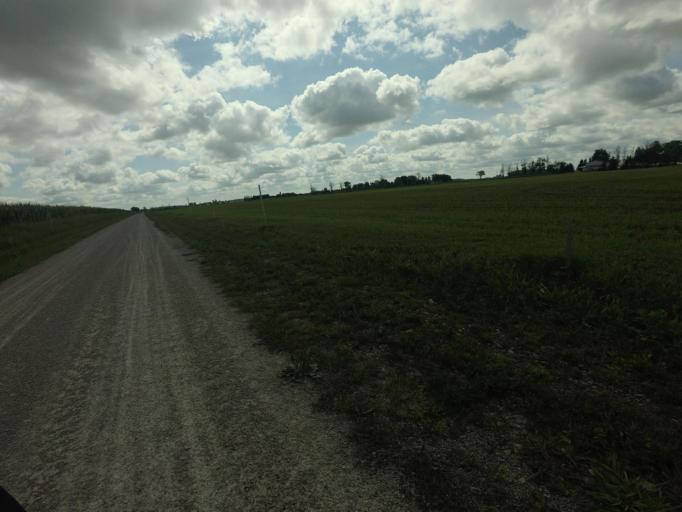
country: CA
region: Ontario
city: Huron East
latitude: 43.6112
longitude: -81.1322
